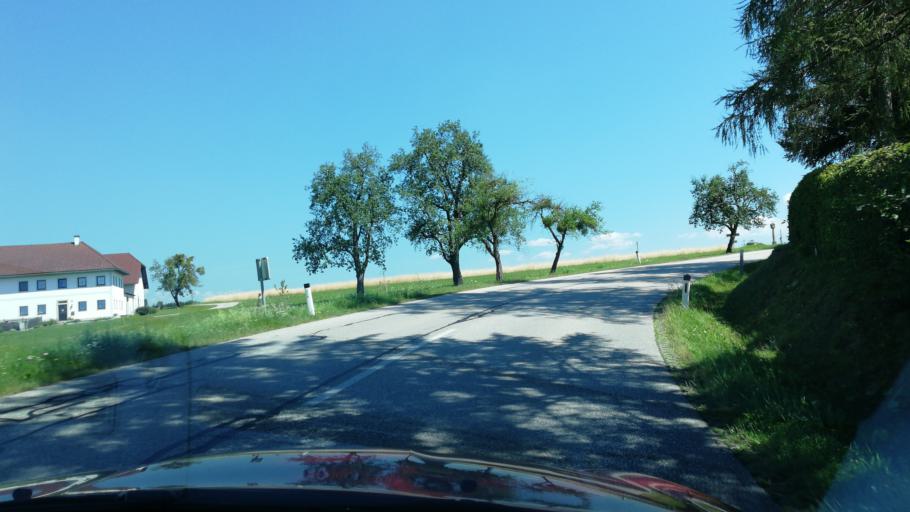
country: AT
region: Upper Austria
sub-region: Politischer Bezirk Rohrbach
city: Kleinzell im Muehlkreis
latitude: 48.4440
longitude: 14.0508
